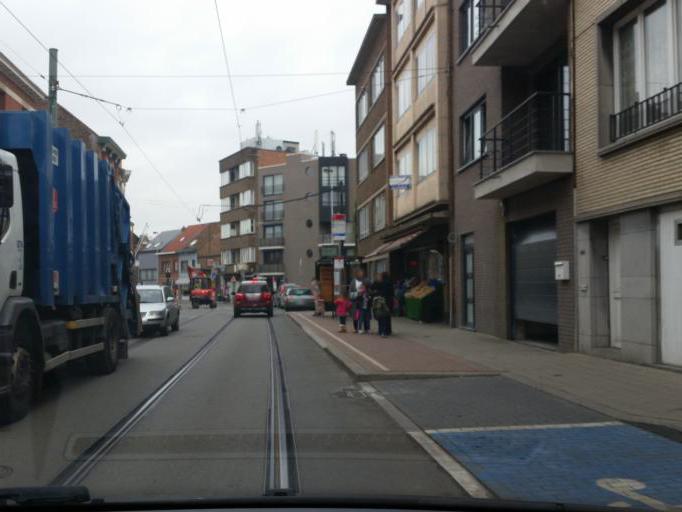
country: BE
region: Flanders
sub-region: Provincie Vlaams-Brabant
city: Drogenbos
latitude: 50.7965
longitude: 4.3212
